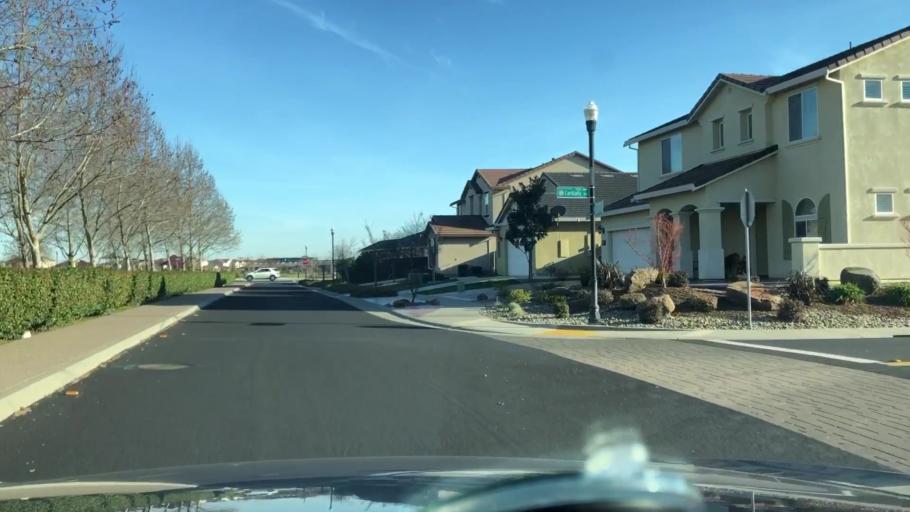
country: US
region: California
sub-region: Sacramento County
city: Laguna
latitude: 38.4020
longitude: -121.4098
